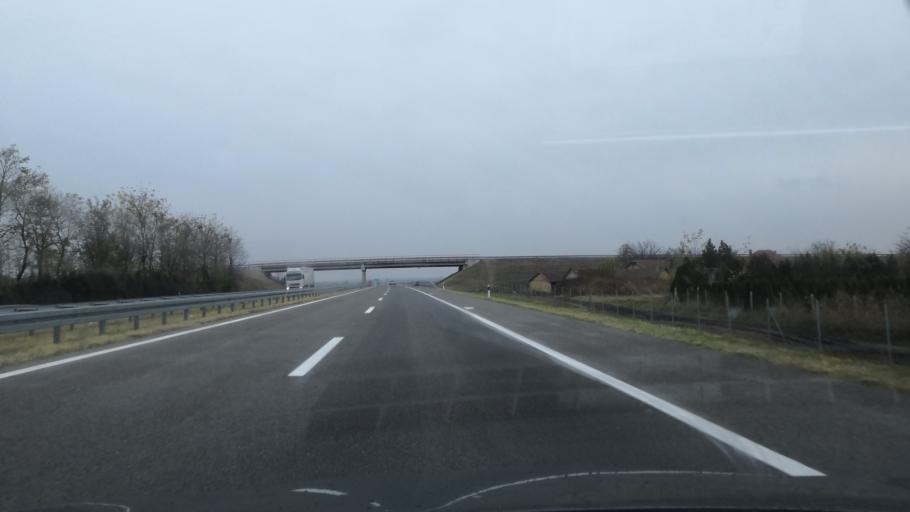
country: HU
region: Csongrad
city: Asotthalom
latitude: 46.0828
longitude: 19.7867
